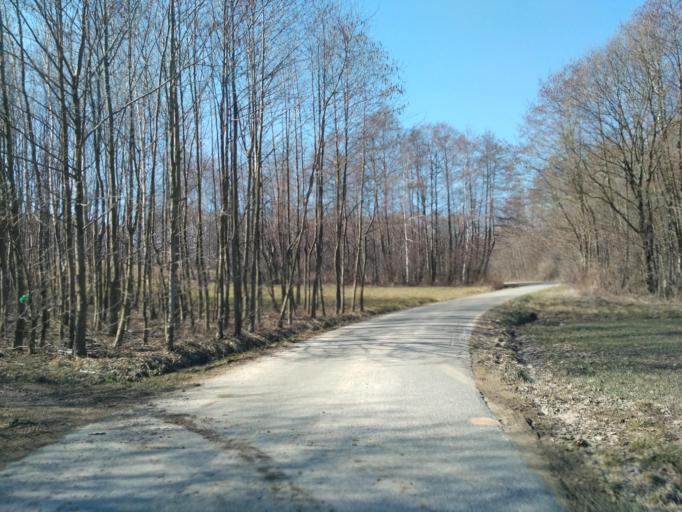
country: PL
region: Subcarpathian Voivodeship
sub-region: Powiat rzeszowski
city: Zglobien
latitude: 49.9874
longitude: 21.8421
